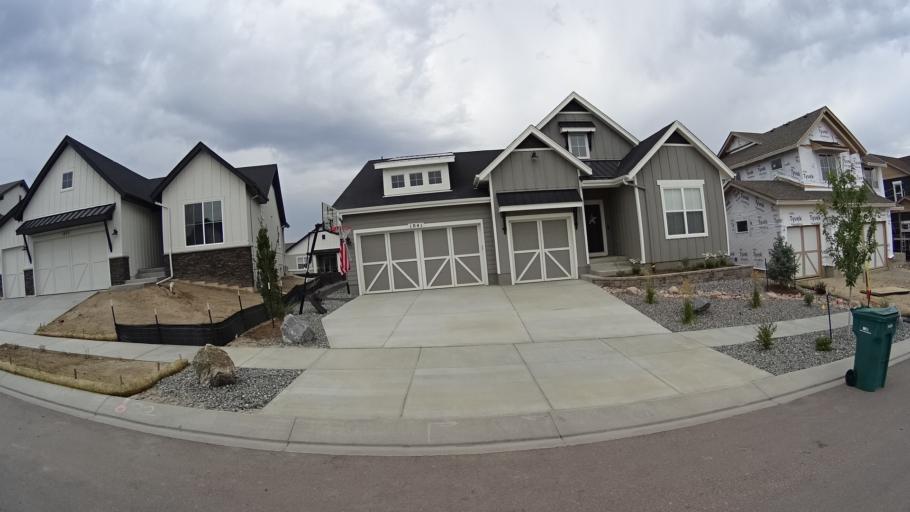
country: US
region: Colorado
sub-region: El Paso County
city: Gleneagle
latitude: 39.0053
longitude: -104.8093
